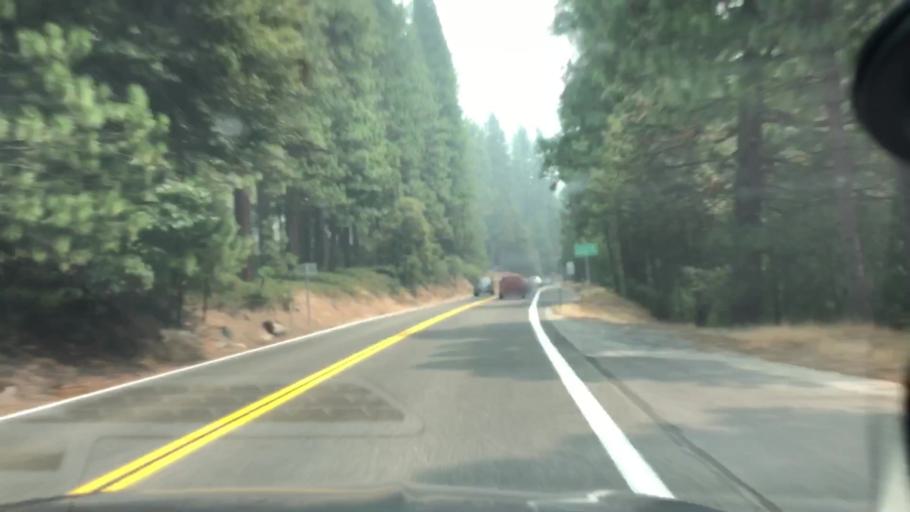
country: US
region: California
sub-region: El Dorado County
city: Pollock Pines
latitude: 38.7736
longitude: -120.3025
